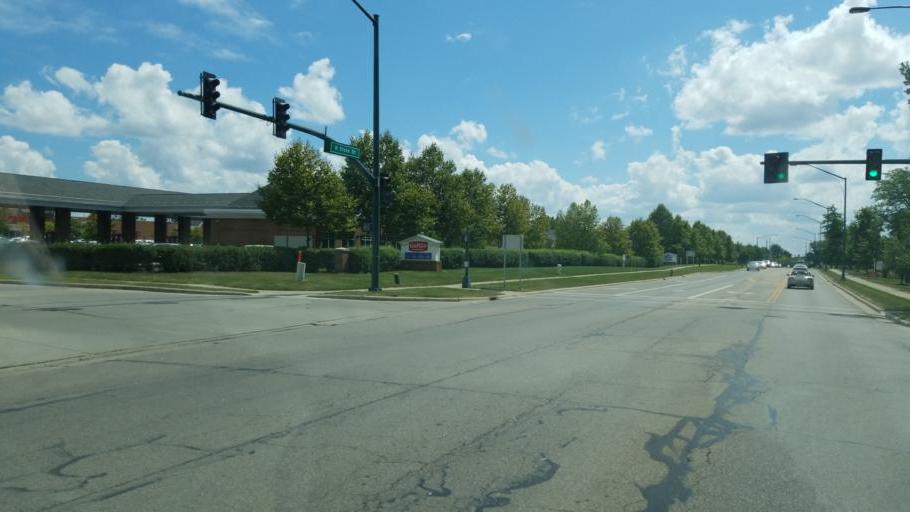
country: US
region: Ohio
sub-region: Franklin County
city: Westerville
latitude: 40.1451
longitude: -82.9251
